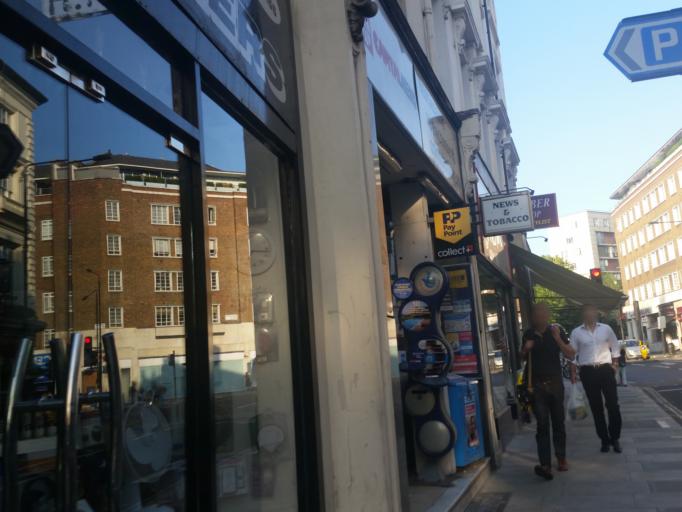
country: GB
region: England
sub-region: Greater London
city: Bayswater
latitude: 51.5156
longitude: -0.1891
